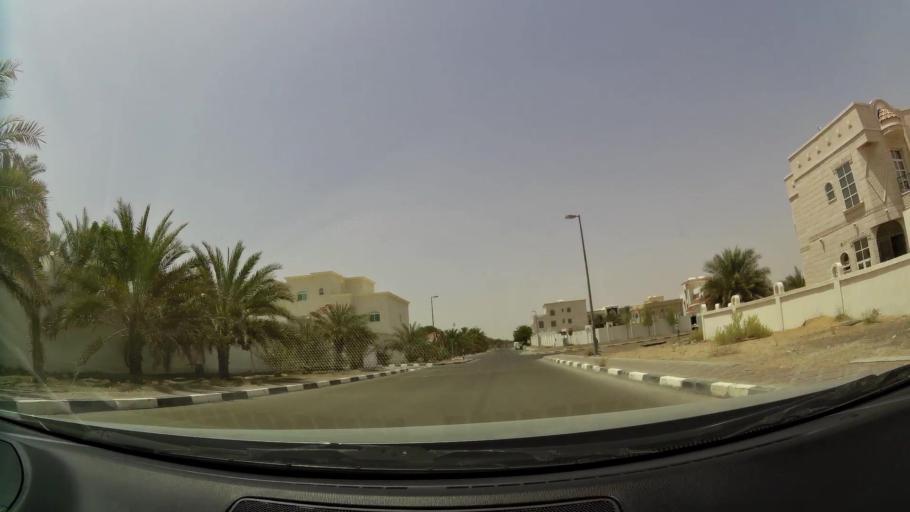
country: AE
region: Abu Dhabi
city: Al Ain
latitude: 24.2001
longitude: 55.7424
